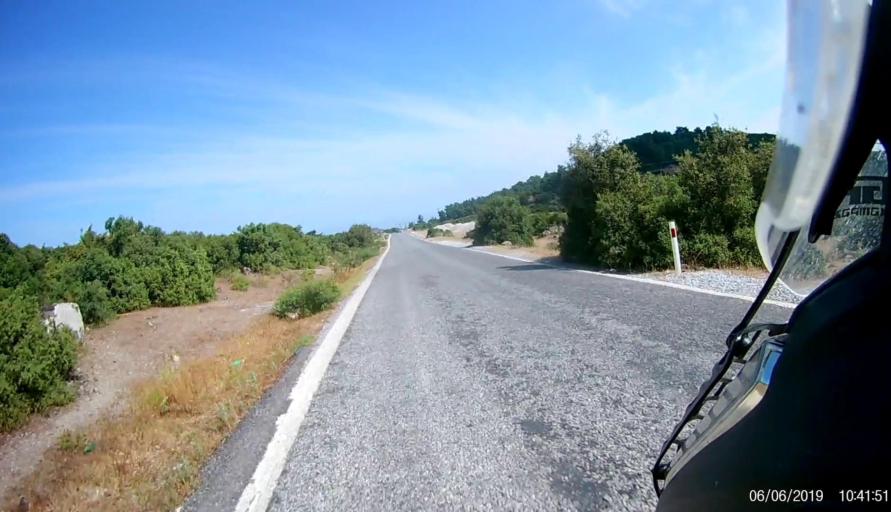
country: TR
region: Canakkale
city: Ayvacik
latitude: 39.5147
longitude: 26.4368
